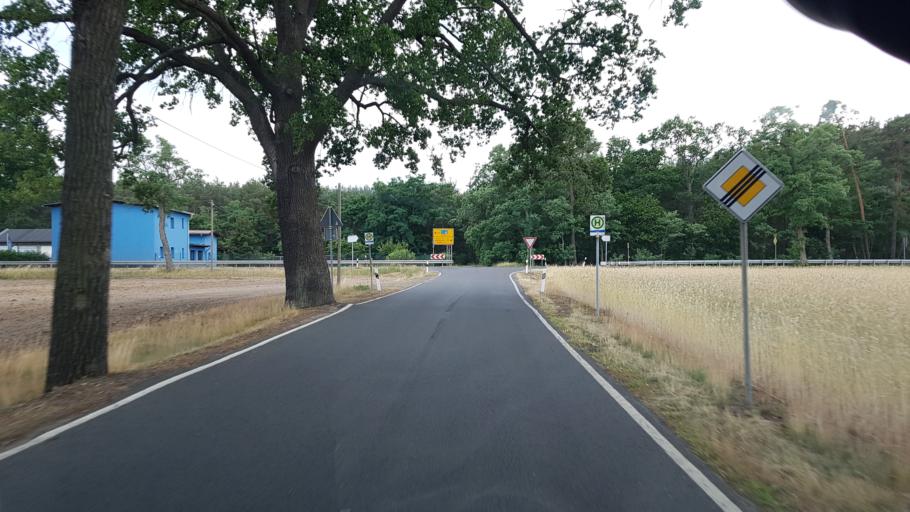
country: DE
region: Brandenburg
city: Kasel-Golzig
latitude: 51.9697
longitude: 13.6843
